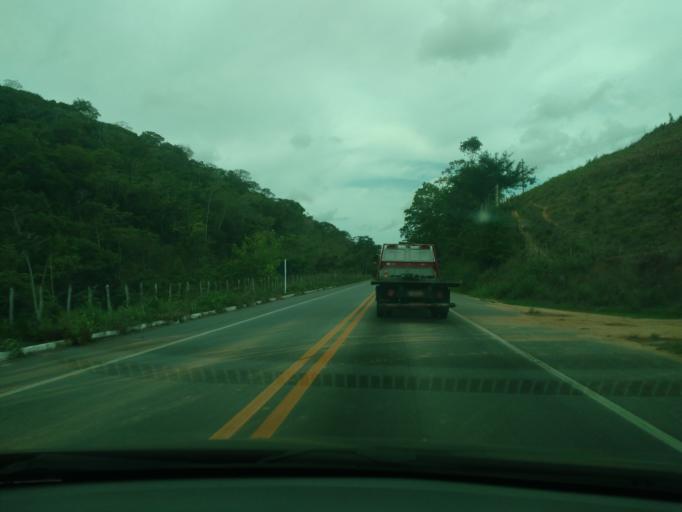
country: BR
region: Alagoas
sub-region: Murici
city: Murici
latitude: -9.3314
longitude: -35.9124
